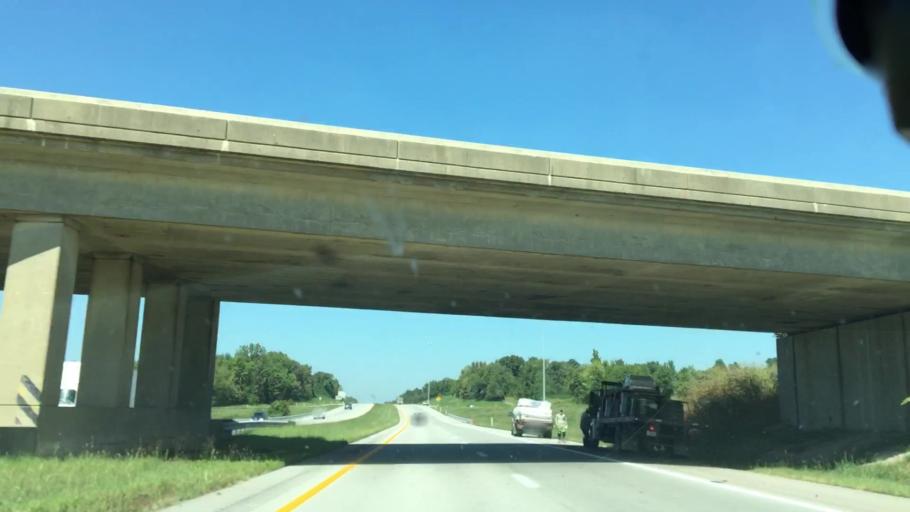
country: US
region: Kentucky
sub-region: Webster County
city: Sebree
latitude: 37.6910
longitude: -87.5138
